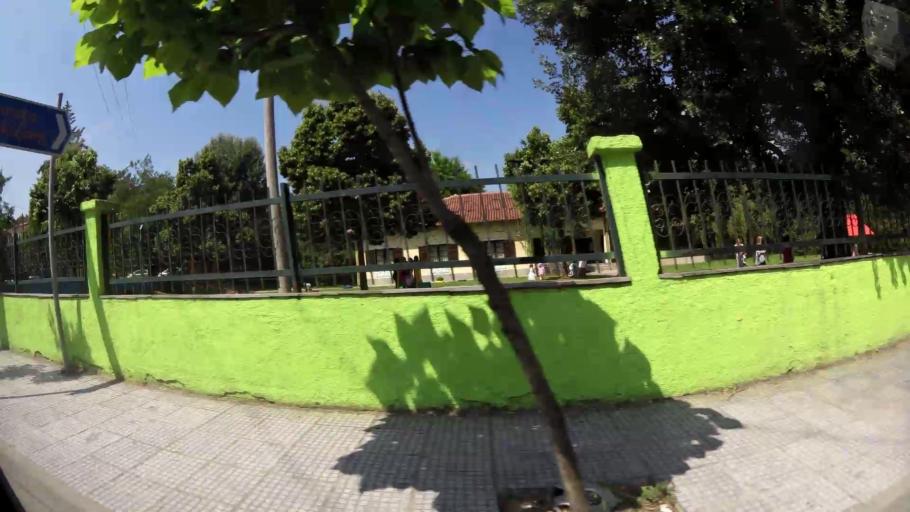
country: GR
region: West Macedonia
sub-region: Nomos Kozanis
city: Kozani
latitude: 40.3113
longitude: 21.7841
